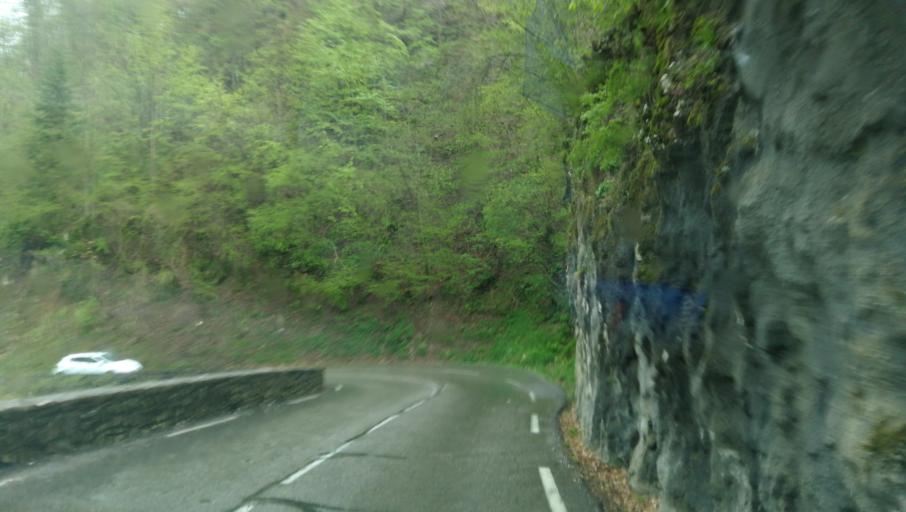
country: FR
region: Rhone-Alpes
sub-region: Departement de l'Isere
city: Meaudre
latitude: 45.0835
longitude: 5.4580
